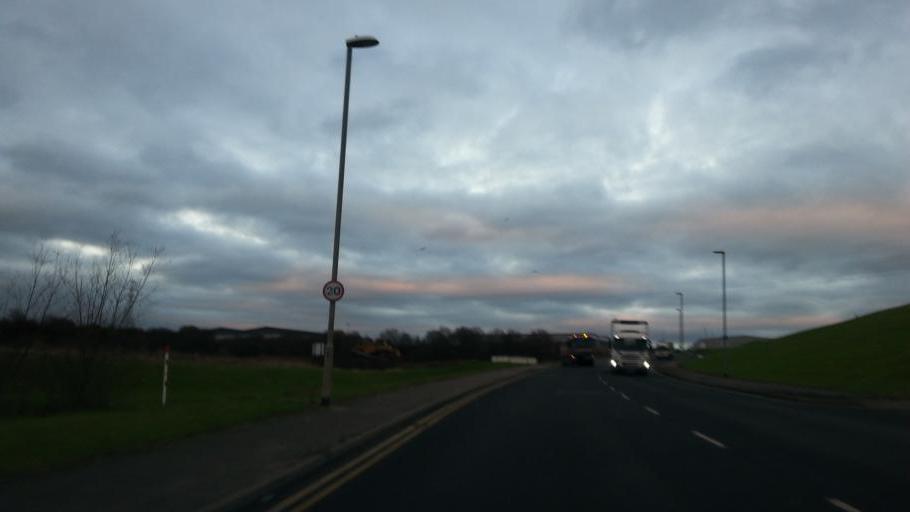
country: GB
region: England
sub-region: Derbyshire
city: Pinxton
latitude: 53.1064
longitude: -1.3074
